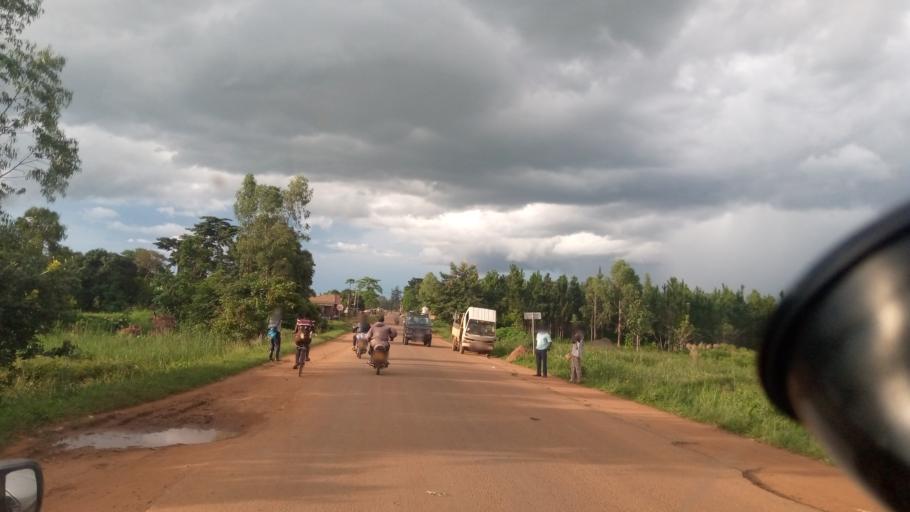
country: UG
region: Northern Region
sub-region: Lira District
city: Lira
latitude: 2.2714
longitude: 32.9158
